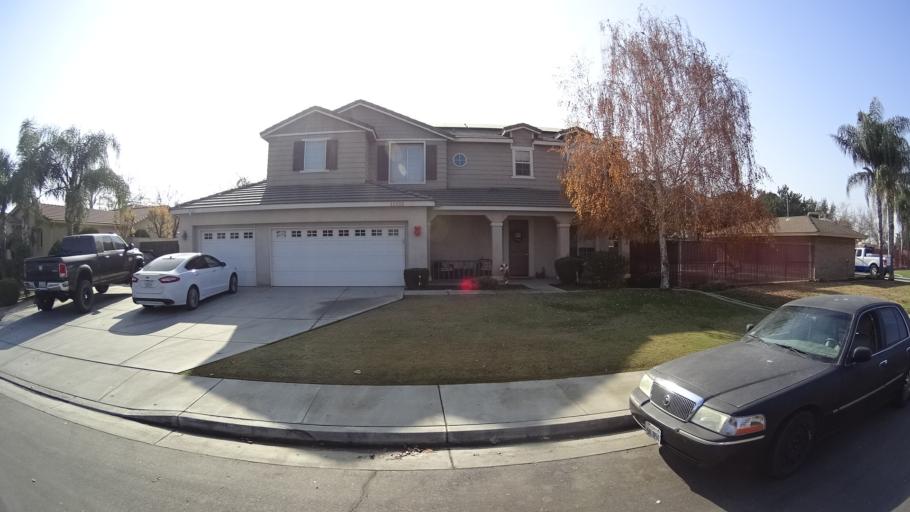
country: US
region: California
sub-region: Kern County
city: Greenacres
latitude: 35.4129
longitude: -119.1261
